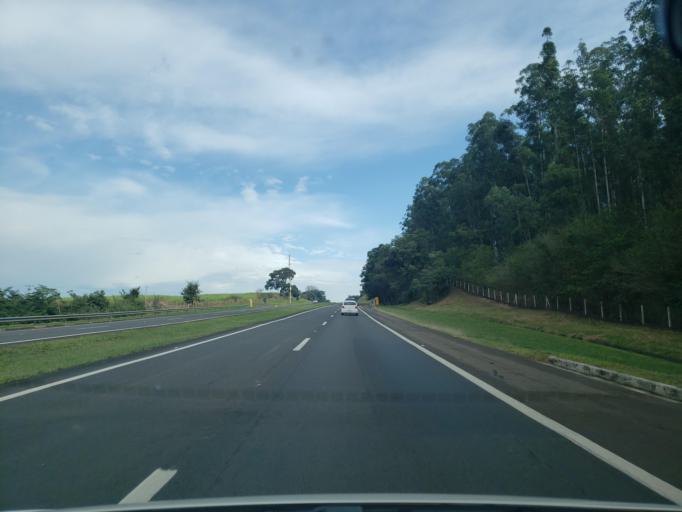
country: BR
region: Sao Paulo
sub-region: Itirapina
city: Itirapina
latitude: -22.2753
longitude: -47.9685
